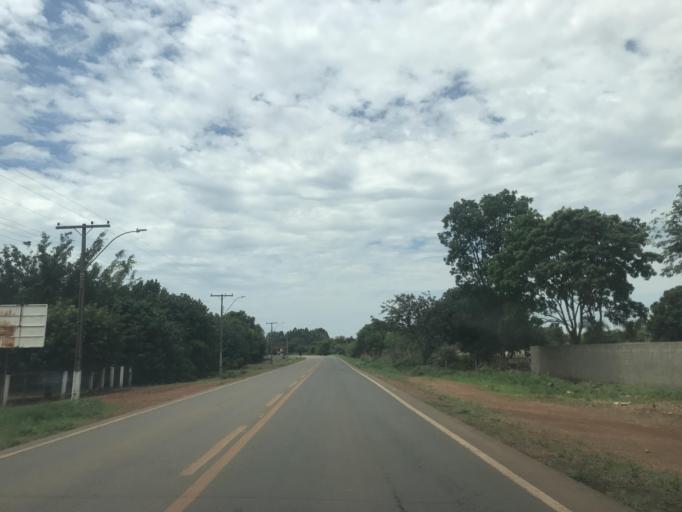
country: BR
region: Goias
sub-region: Luziania
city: Luziania
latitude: -16.3225
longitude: -48.0187
